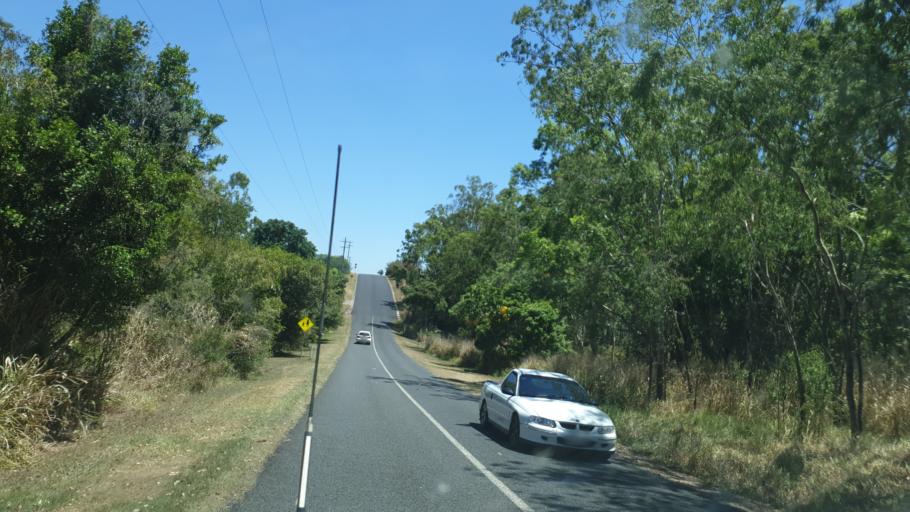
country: AU
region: Queensland
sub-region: Tablelands
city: Atherton
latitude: -17.2653
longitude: 145.4905
